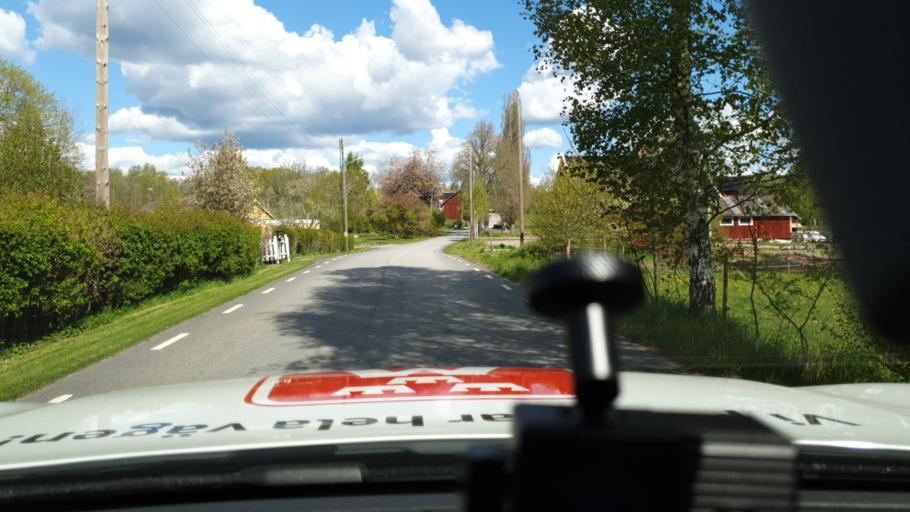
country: SE
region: Kalmar
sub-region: Vasterviks Kommun
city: Ankarsrum
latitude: 57.7786
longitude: 16.1519
